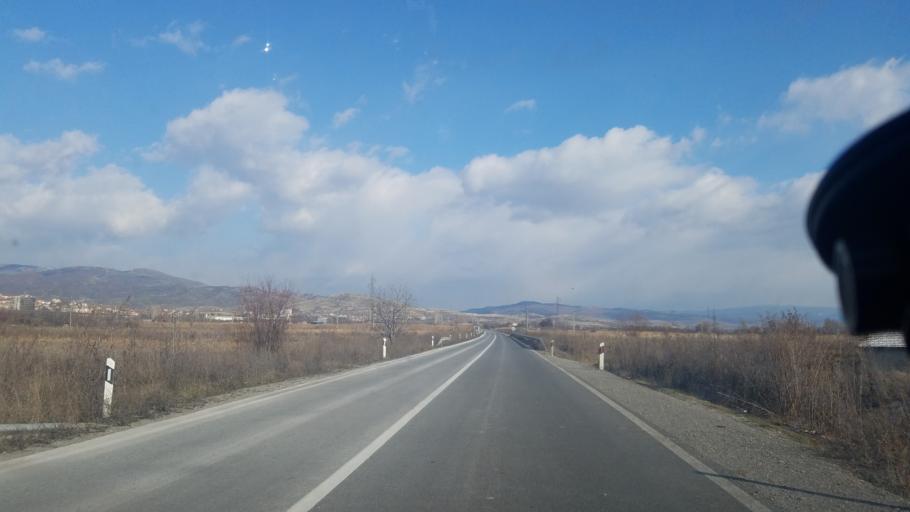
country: MK
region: Kocani
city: Kochani
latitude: 41.9041
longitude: 22.4181
